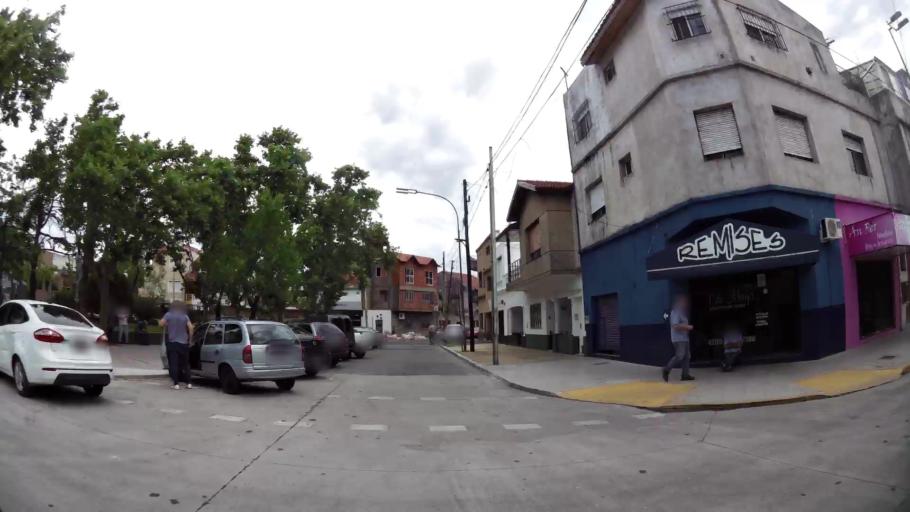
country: AR
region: Buenos Aires
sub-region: Partido de Lanus
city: Lanus
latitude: -34.6759
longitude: -58.4029
